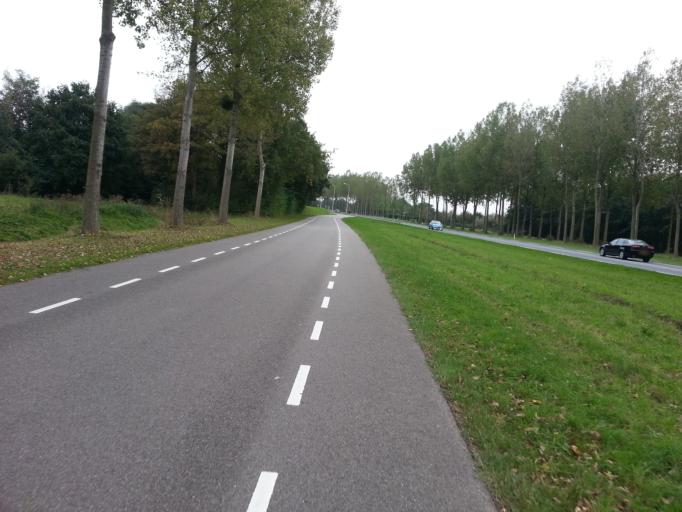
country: NL
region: South Holland
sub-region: Gemeente Brielle
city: Brielle
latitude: 51.9198
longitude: 4.1064
